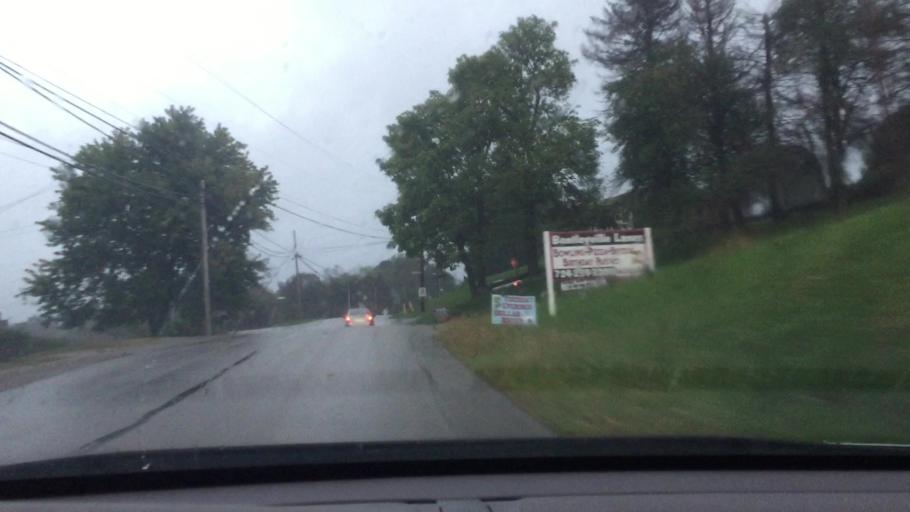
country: US
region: Pennsylvania
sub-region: Washington County
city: Bentleyville
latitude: 40.1268
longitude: -80.0021
